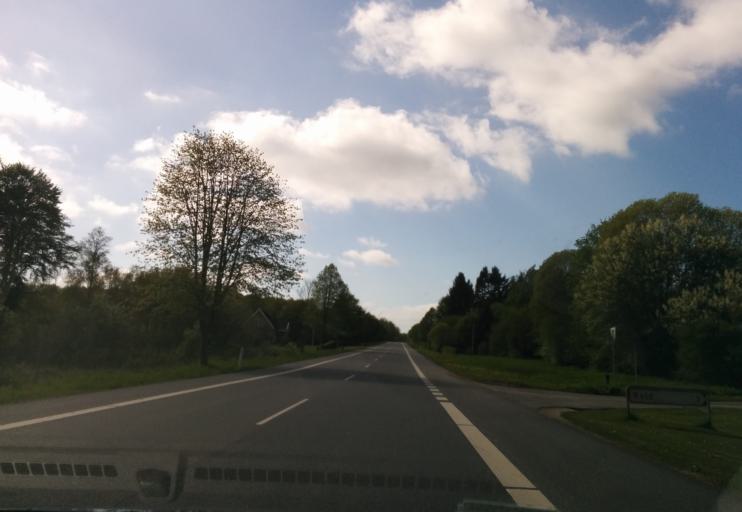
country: DK
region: South Denmark
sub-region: Assens Kommune
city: Arup
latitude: 55.4068
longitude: 10.0784
